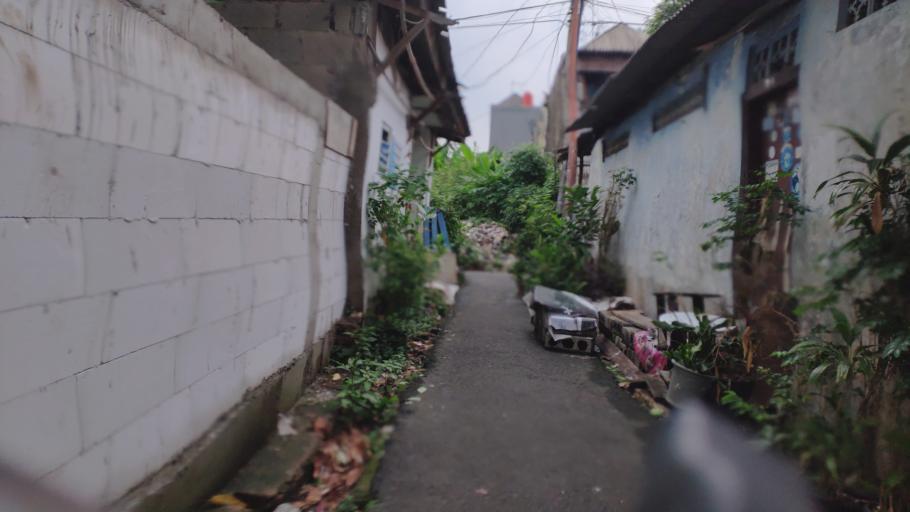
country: ID
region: Jakarta Raya
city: Jakarta
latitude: -6.2175
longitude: 106.8385
